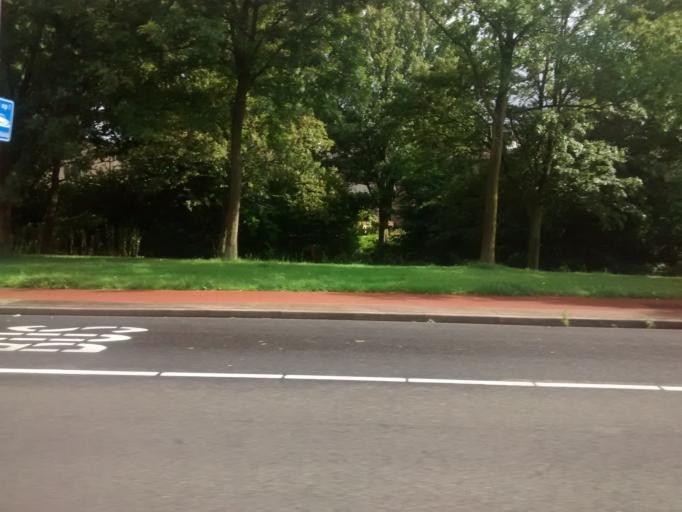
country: NL
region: Utrecht
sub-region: Gemeente Nieuwegein
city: Nieuwegein
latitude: 52.0424
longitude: 5.0929
